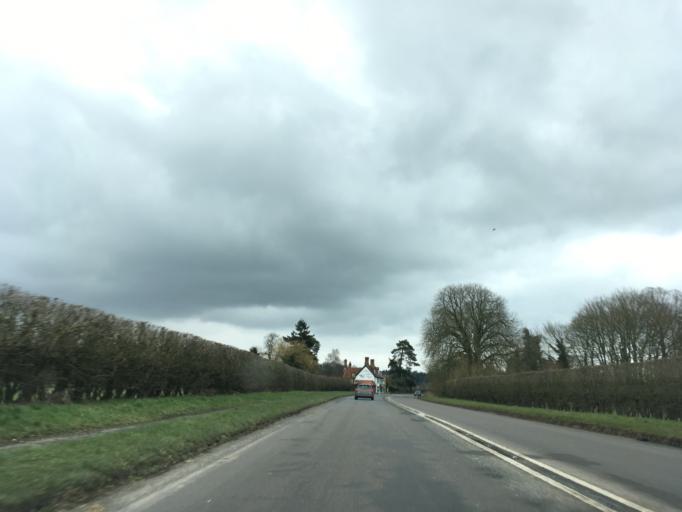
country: GB
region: England
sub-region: West Berkshire
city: Kintbury
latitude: 51.4129
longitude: -1.4178
